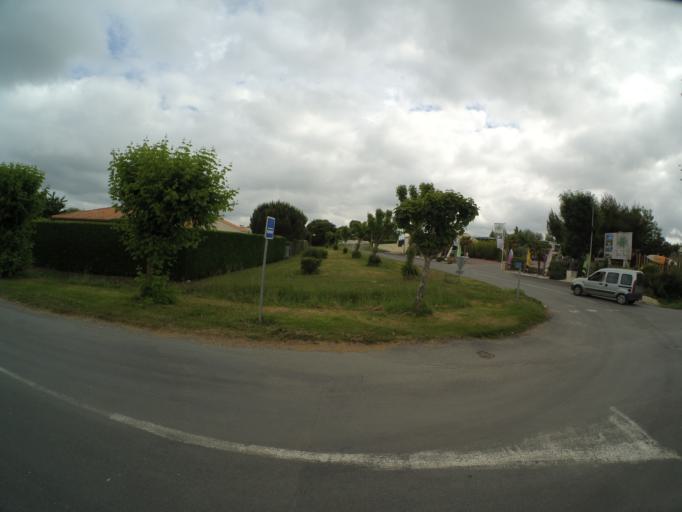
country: FR
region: Poitou-Charentes
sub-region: Departement de la Charente-Maritime
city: Saint-Laurent-de-la-Pree
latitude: 45.9904
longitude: -1.0202
